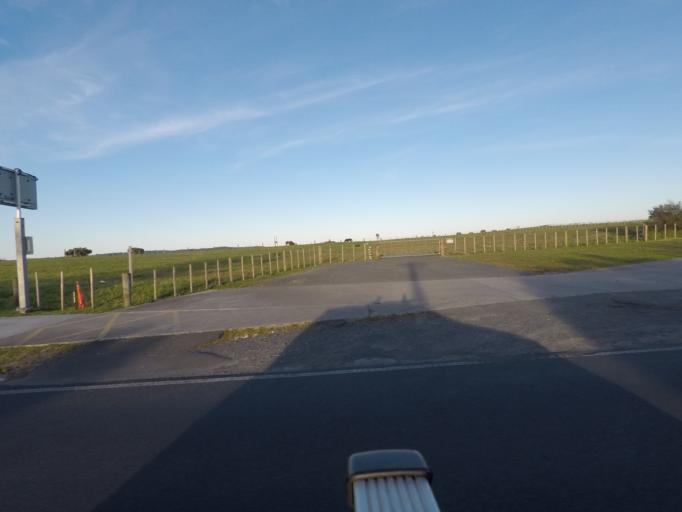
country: NZ
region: Auckland
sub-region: Auckland
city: Rosebank
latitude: -36.8548
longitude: 174.6514
